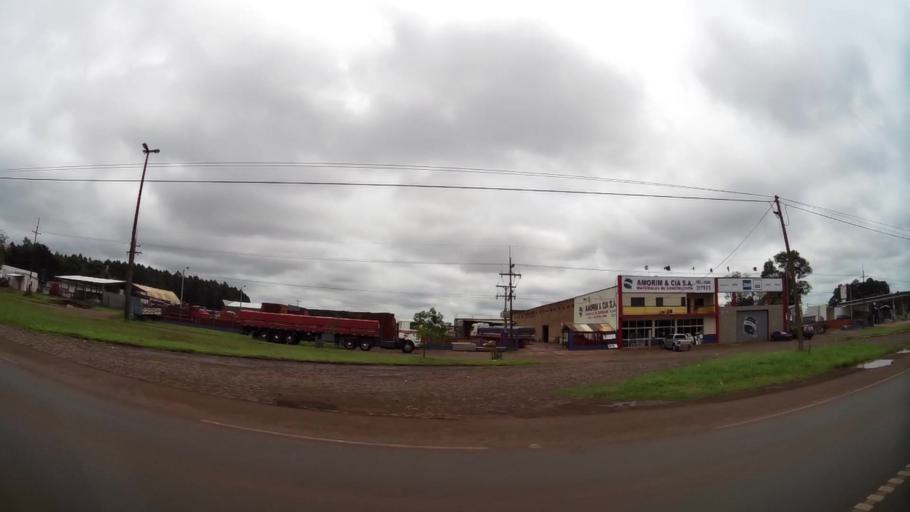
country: PY
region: Alto Parana
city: Presidente Franco
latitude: -25.4913
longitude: -54.7531
